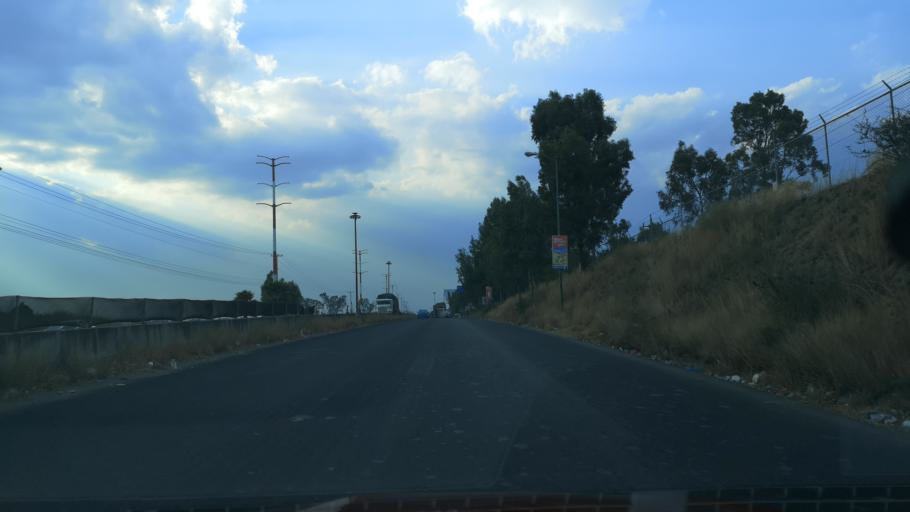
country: MX
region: Puebla
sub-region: Juan C. Bonilla
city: Santa Maria Zacatepec
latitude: 19.1289
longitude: -98.3706
